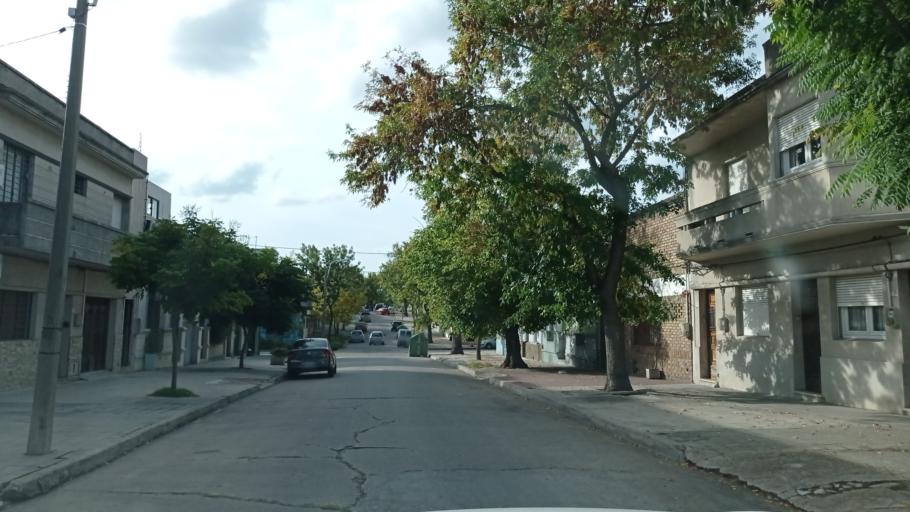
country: UY
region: Montevideo
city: Montevideo
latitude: -34.8874
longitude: -56.1749
